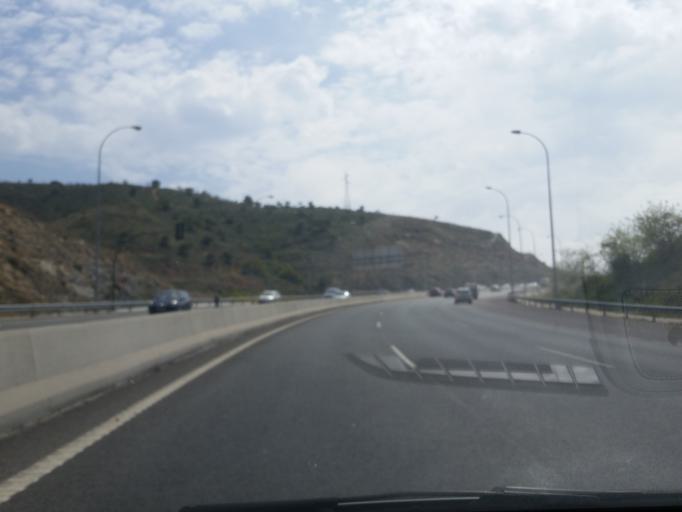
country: ES
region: Andalusia
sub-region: Provincia de Malaga
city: Malaga
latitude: 36.7558
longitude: -4.4175
